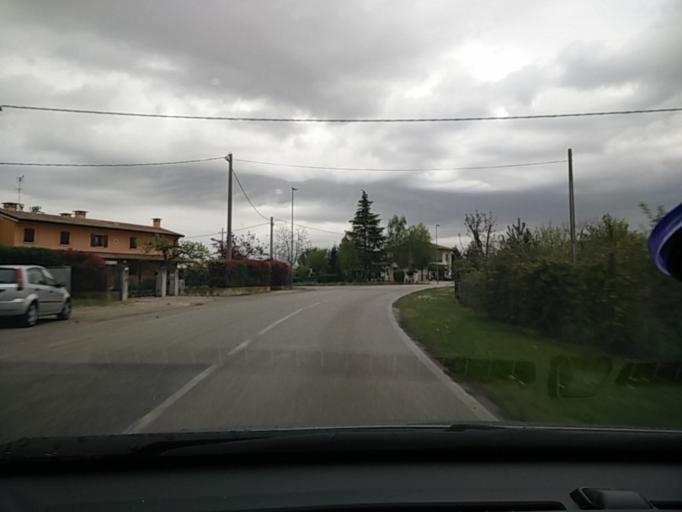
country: IT
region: Veneto
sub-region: Provincia di Treviso
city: Roncade
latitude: 45.6224
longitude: 12.3597
